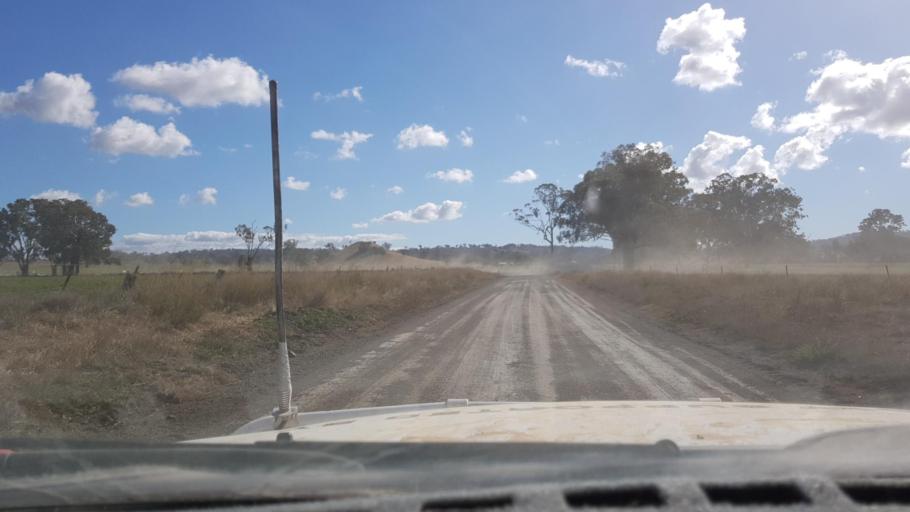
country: AU
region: New South Wales
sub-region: Tamworth Municipality
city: Manilla
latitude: -30.5879
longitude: 150.4889
